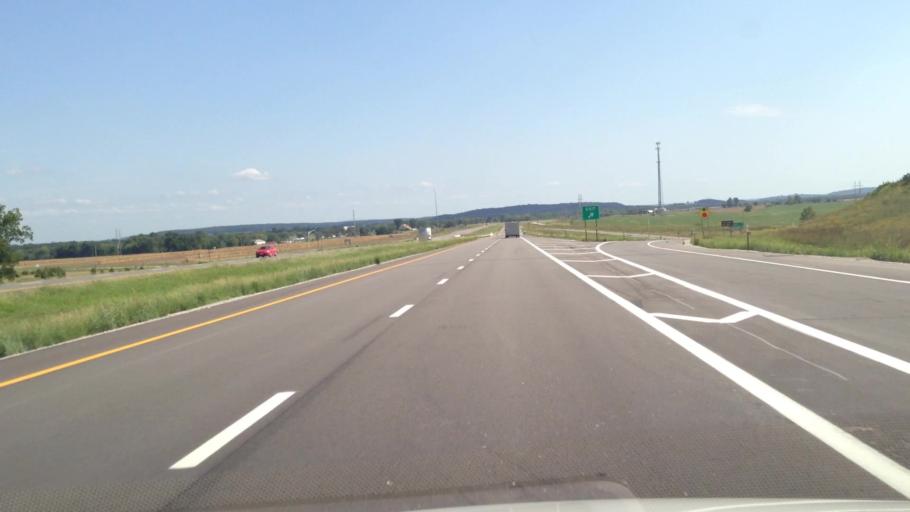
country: US
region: Kansas
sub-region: Linn County
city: La Cygne
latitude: 38.3482
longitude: -94.6845
